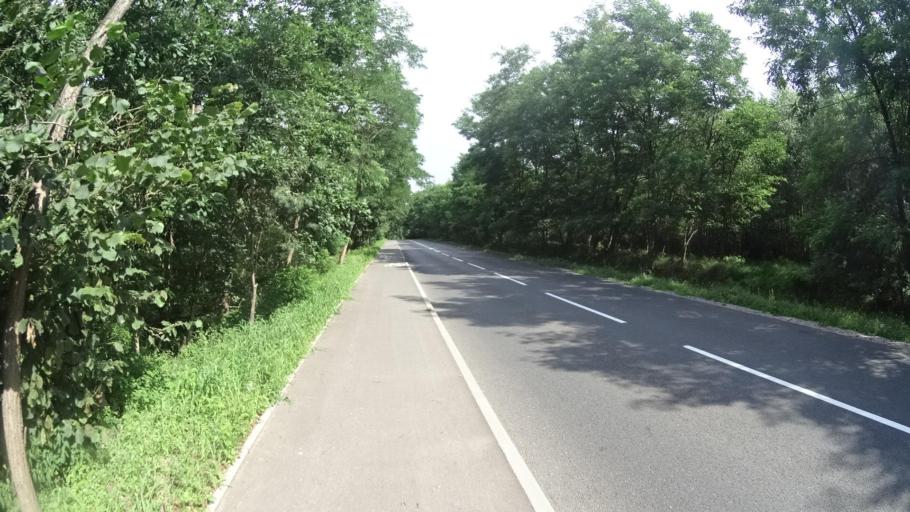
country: PL
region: Masovian Voivodeship
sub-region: Powiat piaseczynski
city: Tarczyn
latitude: 52.0276
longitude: 20.7837
